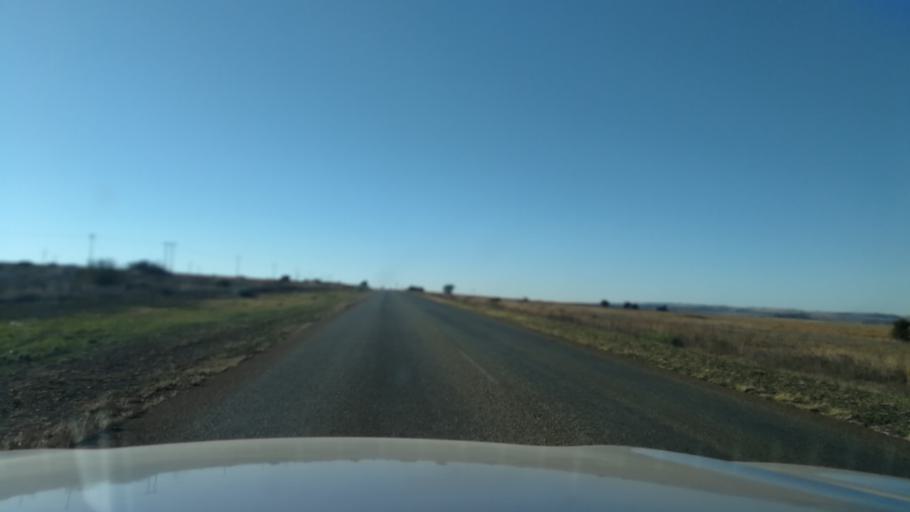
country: ZA
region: North-West
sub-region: Bojanala Platinum District Municipality
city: Rustenburg
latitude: -25.9895
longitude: 27.2834
